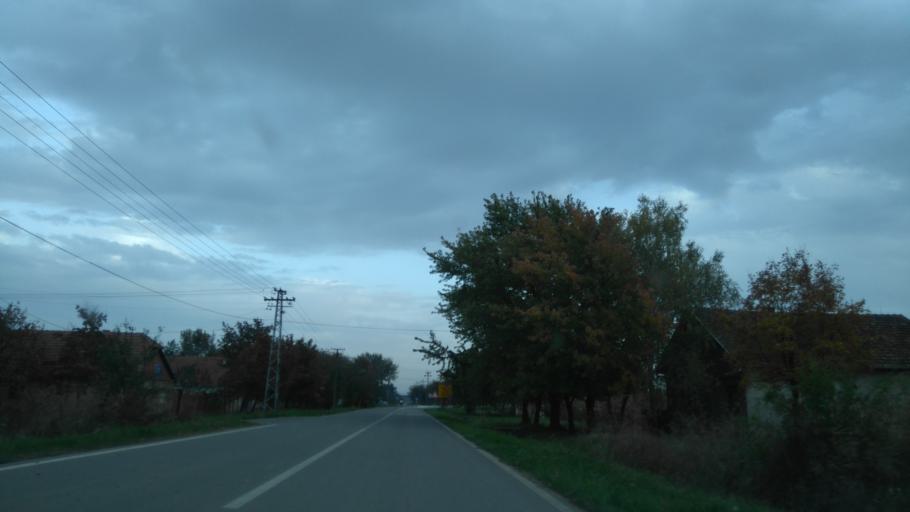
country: RS
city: Mol
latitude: 45.7541
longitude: 20.1284
